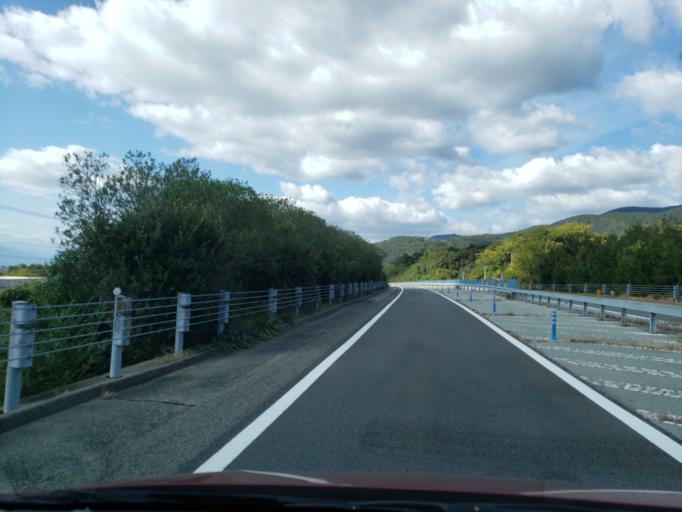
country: JP
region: Tokushima
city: Kamojimacho-jogejima
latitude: 34.1221
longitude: 134.3651
